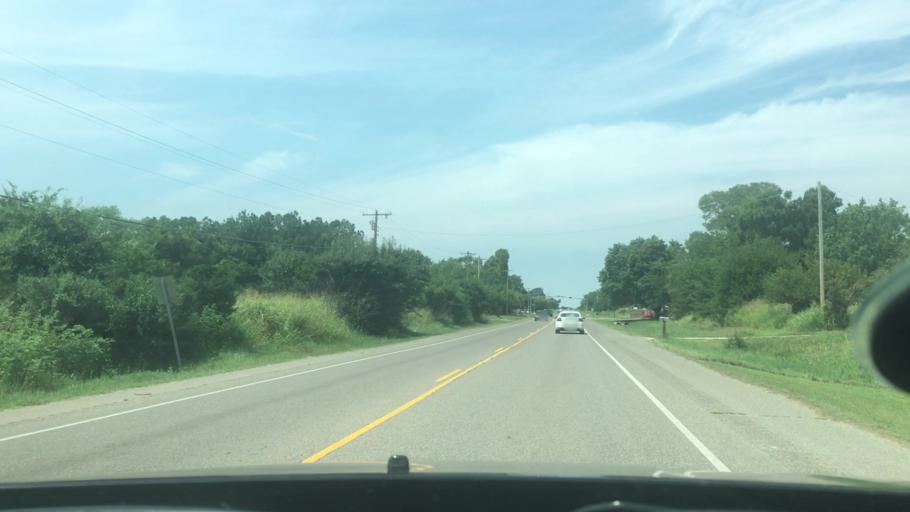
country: US
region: Oklahoma
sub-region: Pottawatomie County
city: Shawnee
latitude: 35.3332
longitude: -96.8561
